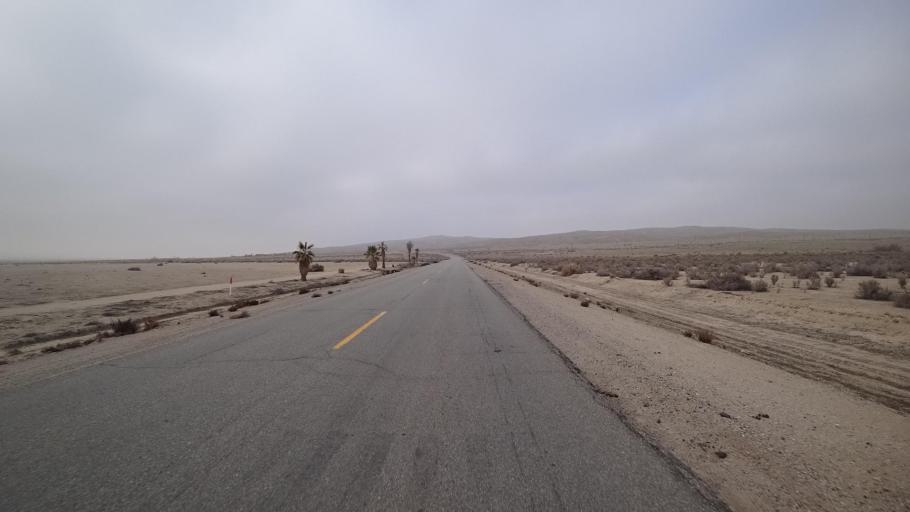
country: US
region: California
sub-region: Kern County
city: Maricopa
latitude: 35.1253
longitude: -119.3632
